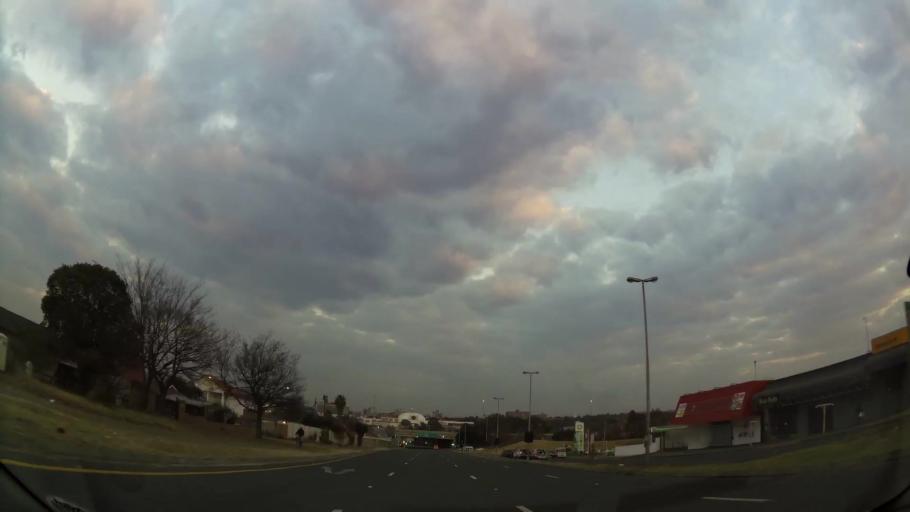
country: ZA
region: Gauteng
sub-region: Ekurhuleni Metropolitan Municipality
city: Benoni
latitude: -26.1796
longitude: 28.3115
